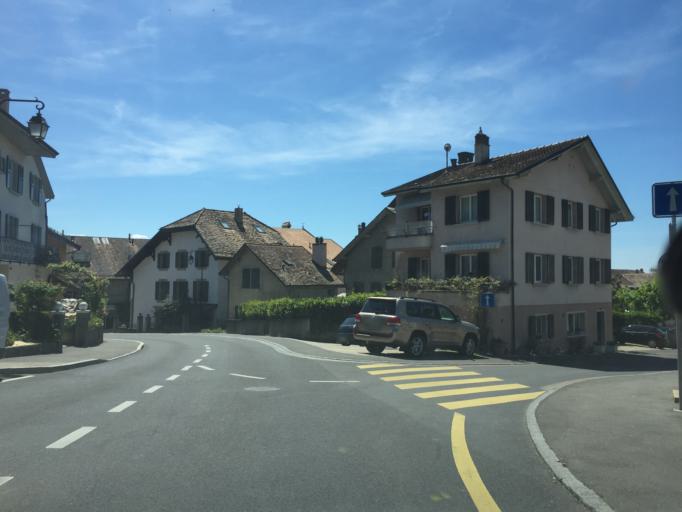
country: CH
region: Vaud
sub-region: Morges District
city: Aubonne
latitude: 46.4854
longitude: 6.4194
